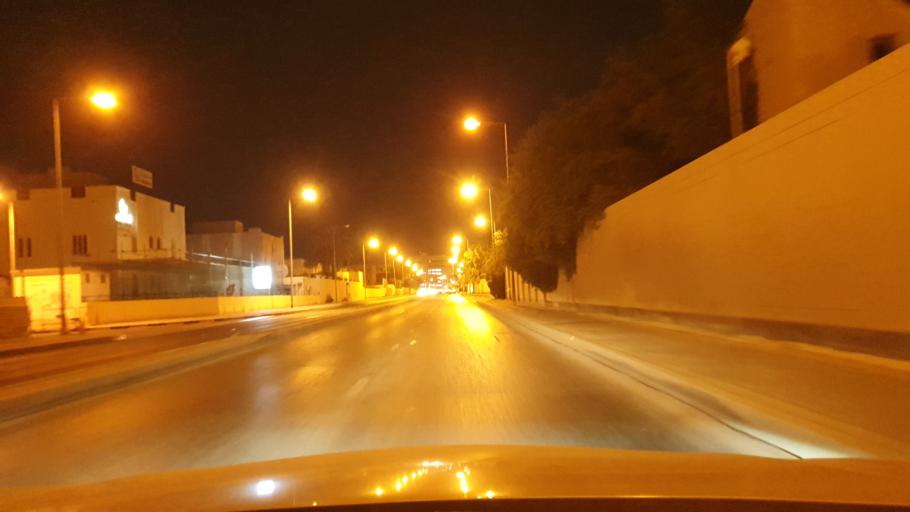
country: BH
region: Manama
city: Manama
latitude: 26.2160
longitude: 50.5808
